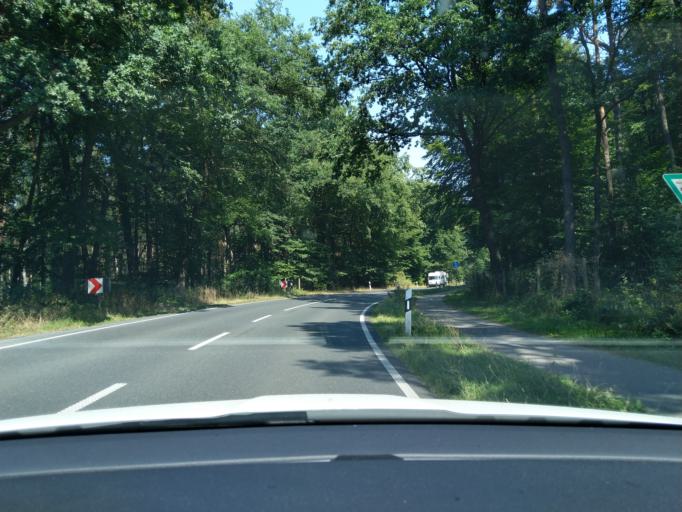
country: DE
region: North Rhine-Westphalia
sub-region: Regierungsbezirk Koln
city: Wassenberg
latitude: 51.1358
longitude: 6.1939
